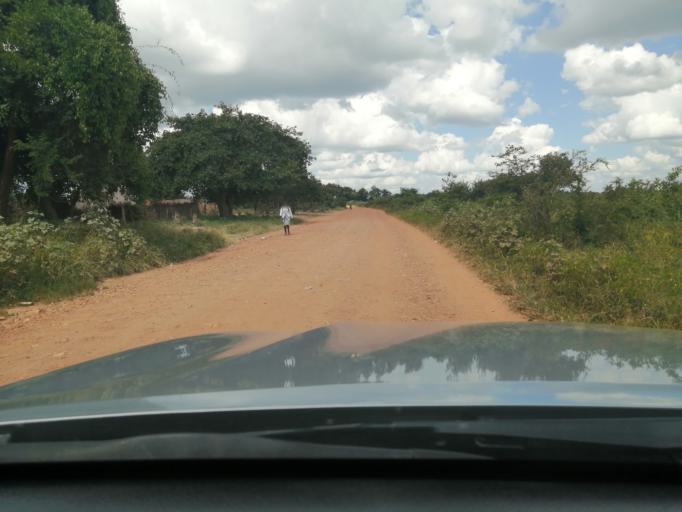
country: ZM
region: Lusaka
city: Lusaka
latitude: -15.1936
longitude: 27.9835
